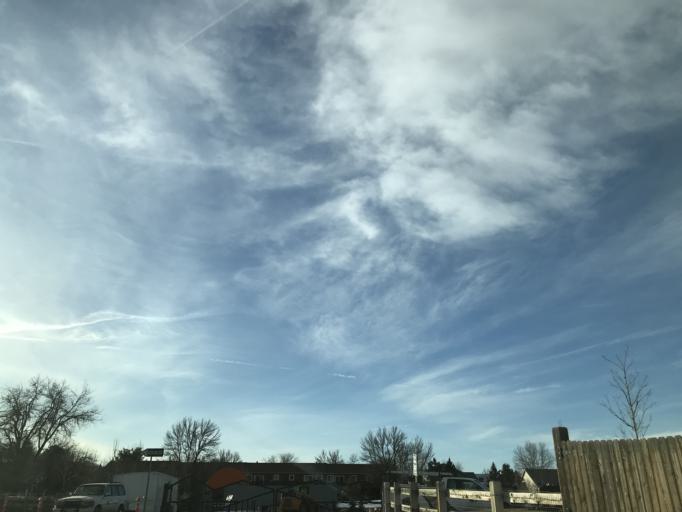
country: US
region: Colorado
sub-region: Arapahoe County
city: Columbine Valley
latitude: 39.5926
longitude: -105.0247
